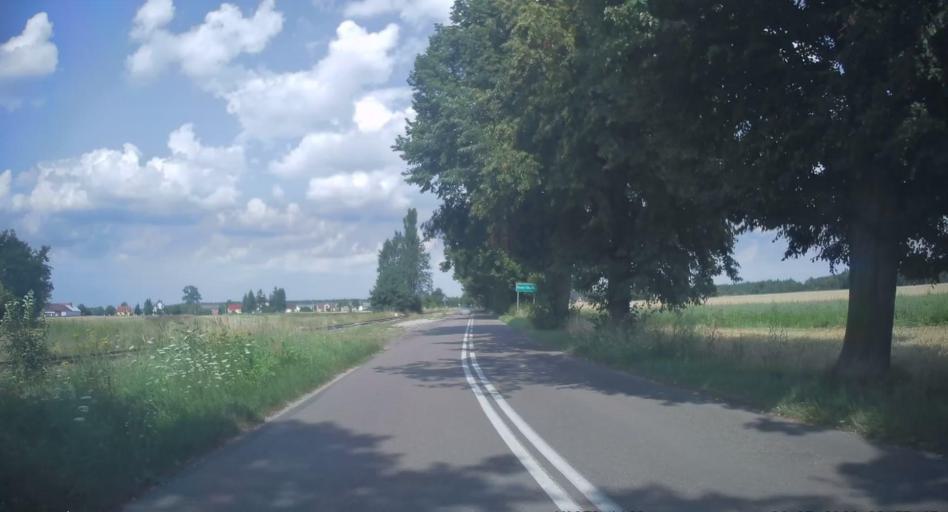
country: PL
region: Lodz Voivodeship
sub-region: Powiat tomaszowski
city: Lubochnia
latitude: 51.5699
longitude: 20.1012
